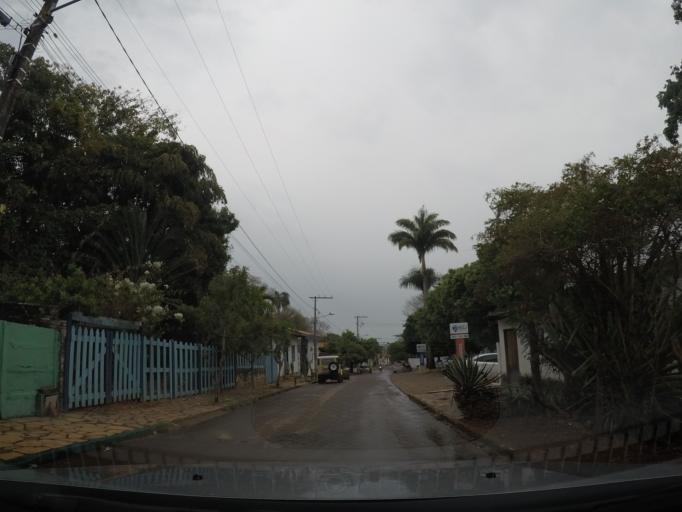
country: BR
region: Goias
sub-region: Pirenopolis
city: Pirenopolis
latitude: -15.8495
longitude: -48.9516
